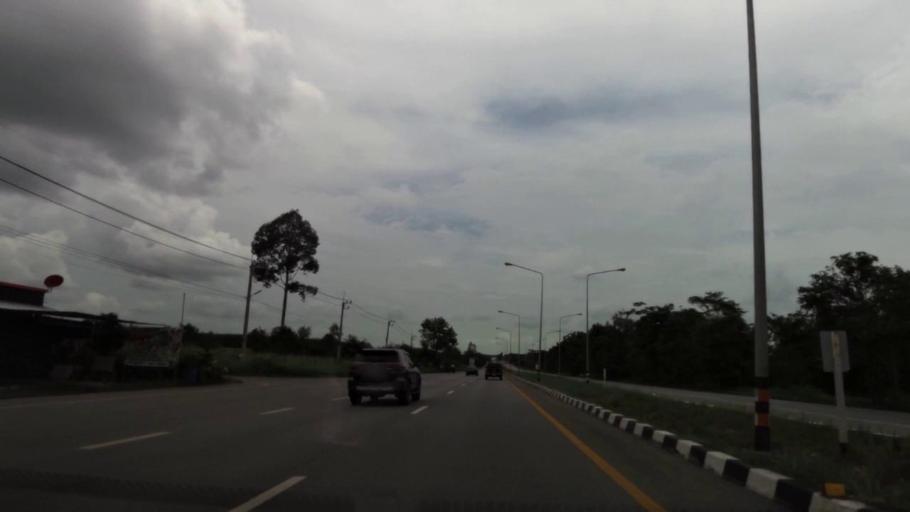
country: TH
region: Chon Buri
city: Nong Yai
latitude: 13.1301
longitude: 101.3549
